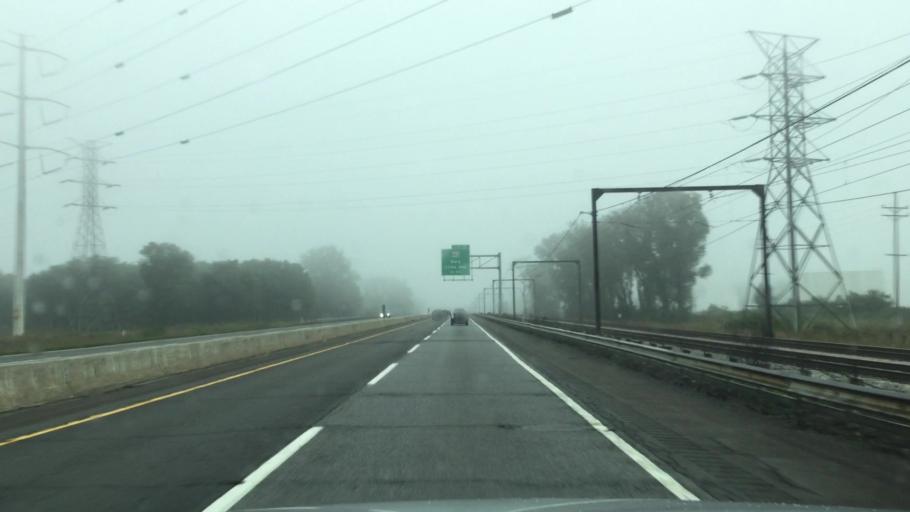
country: US
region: Indiana
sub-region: Lake County
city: East Chicago
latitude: 41.6106
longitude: -87.4438
